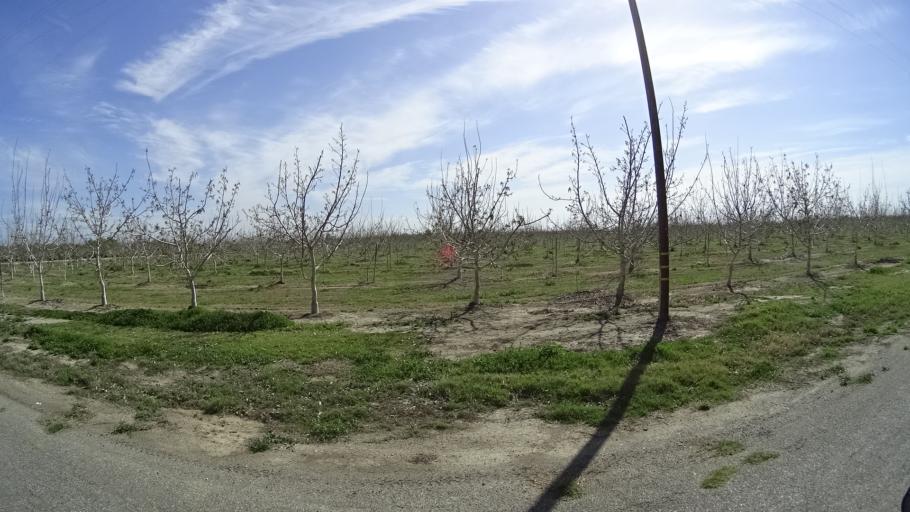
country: US
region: California
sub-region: Glenn County
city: Hamilton City
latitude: 39.6333
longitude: -122.0181
